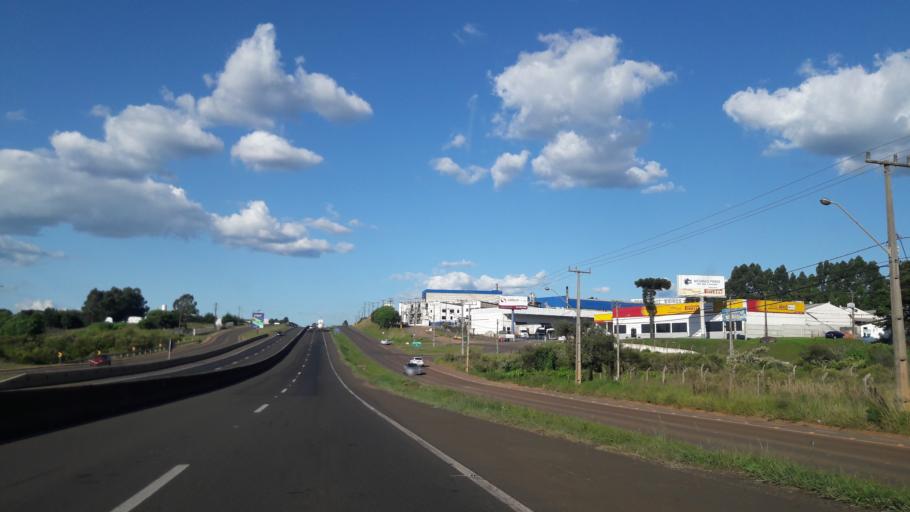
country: BR
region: Parana
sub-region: Guarapuava
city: Guarapuava
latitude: -25.3571
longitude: -51.4630
